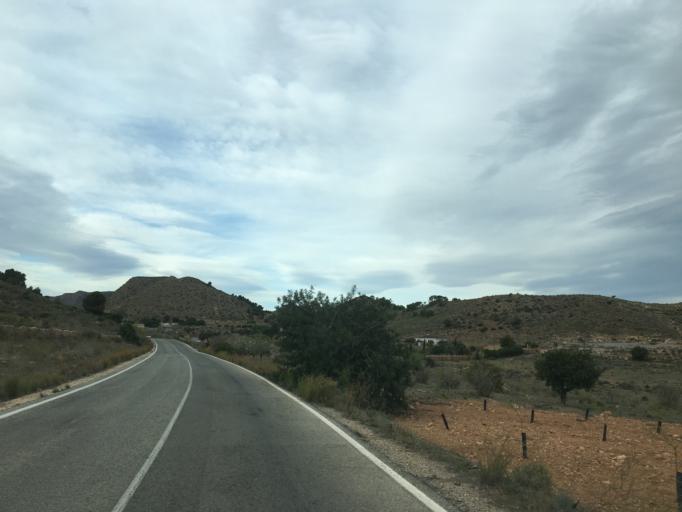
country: ES
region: Murcia
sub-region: Murcia
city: Fuente-Alamo de Murcia
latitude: 37.6124
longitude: -1.1040
